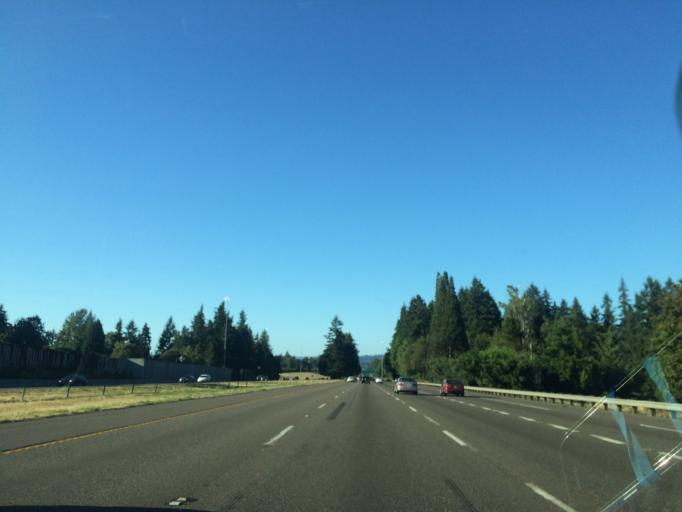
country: US
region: Oregon
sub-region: Washington County
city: Tualatin
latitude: 45.3587
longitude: -122.7619
